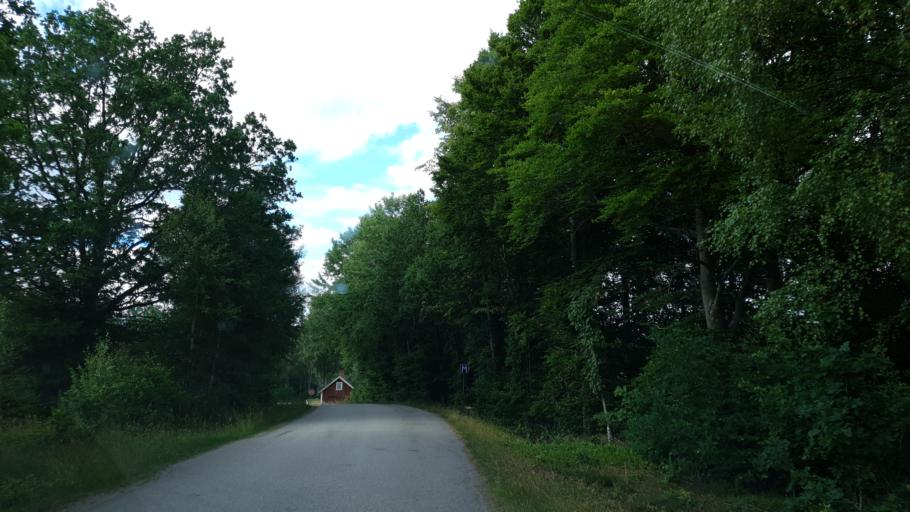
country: SE
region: Kalmar
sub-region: Emmaboda Kommun
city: Emmaboda
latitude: 56.6289
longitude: 15.6446
